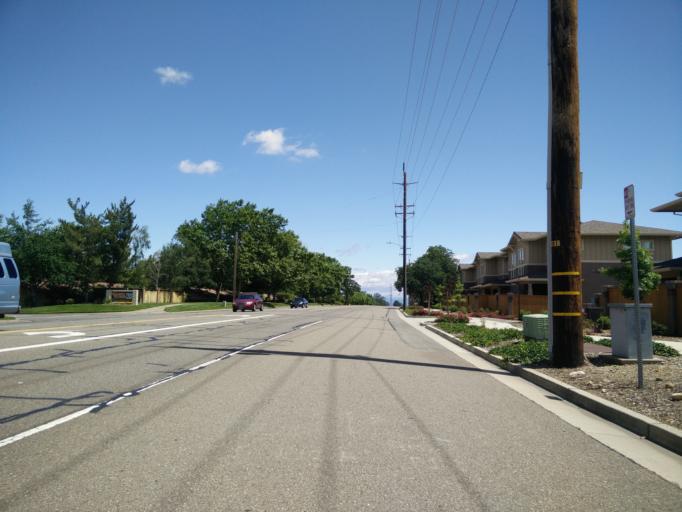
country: US
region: California
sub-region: Shasta County
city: Redding
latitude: 40.5968
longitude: -122.3675
